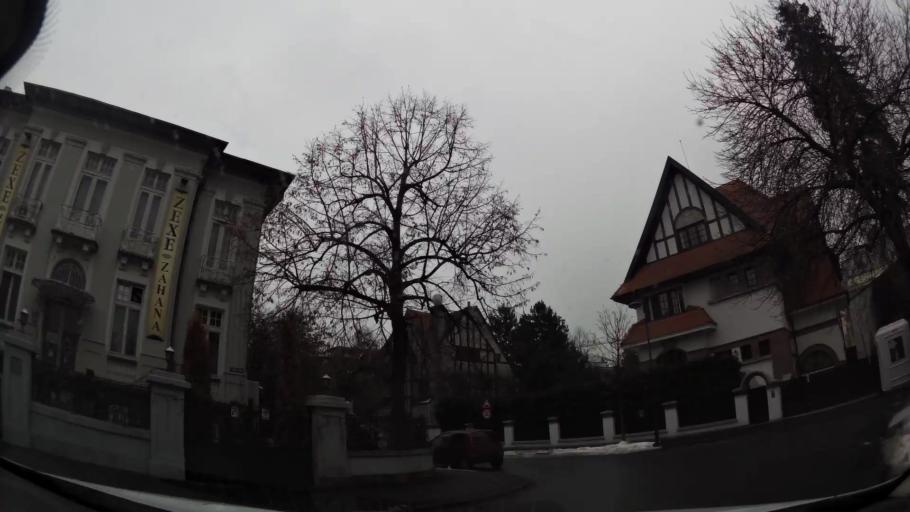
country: RO
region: Bucuresti
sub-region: Municipiul Bucuresti
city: Bucharest
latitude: 44.4597
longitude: 26.0894
